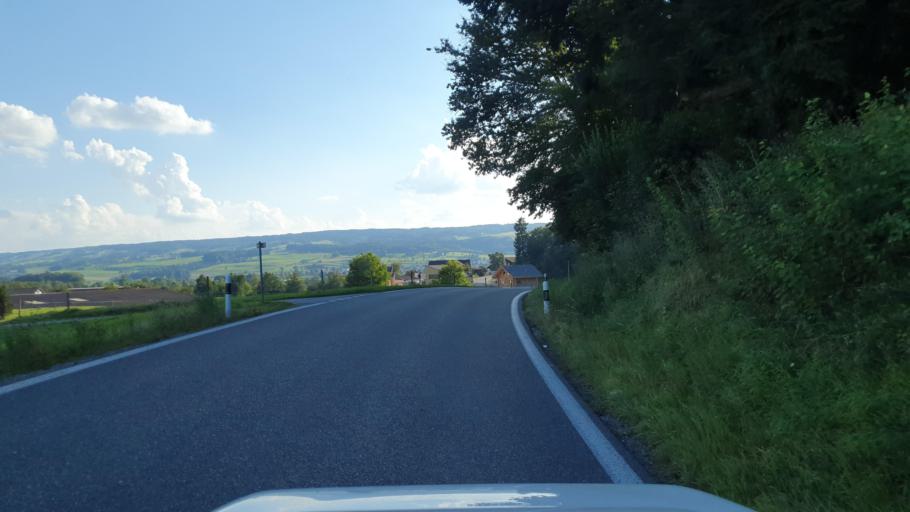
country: CH
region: Aargau
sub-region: Bezirk Muri
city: Waltenschwil
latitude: 47.3137
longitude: 8.3338
